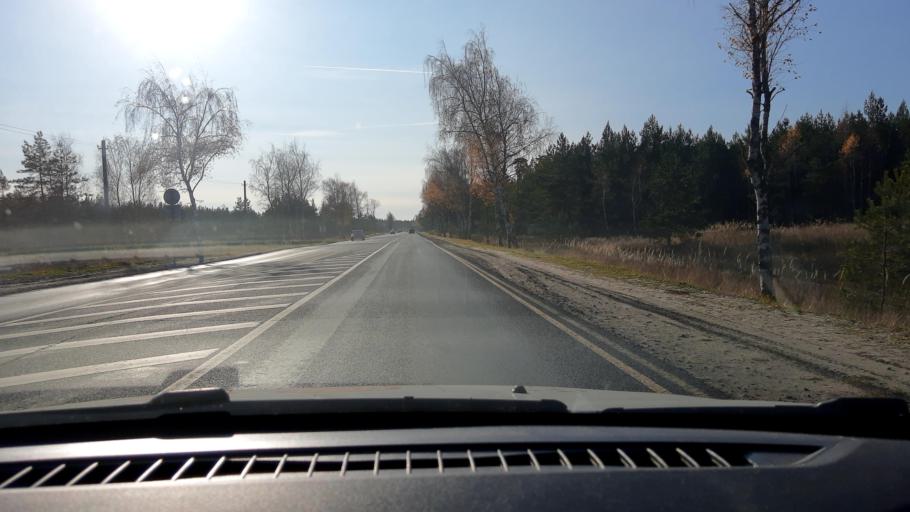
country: RU
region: Nizjnij Novgorod
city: Dzerzhinsk
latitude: 56.2832
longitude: 43.4754
